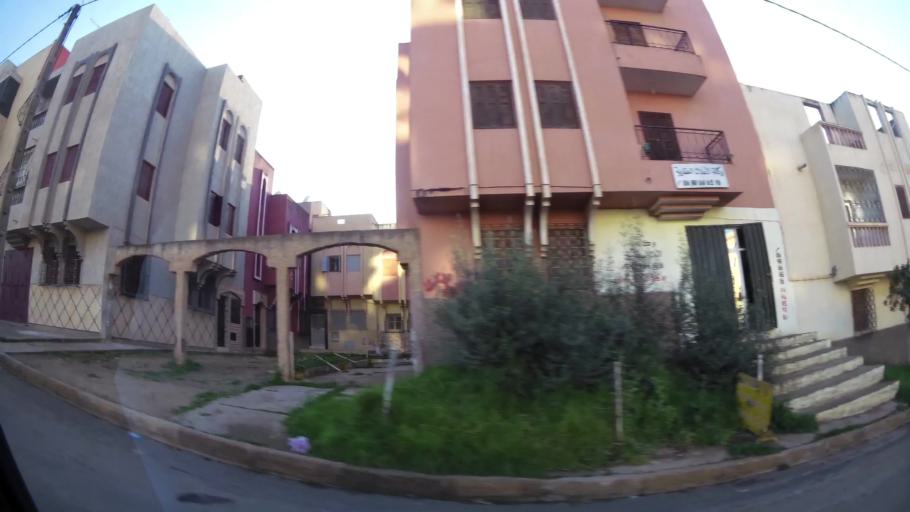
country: MA
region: Chaouia-Ouardigha
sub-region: Settat Province
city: Settat
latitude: 32.9922
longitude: -7.6060
